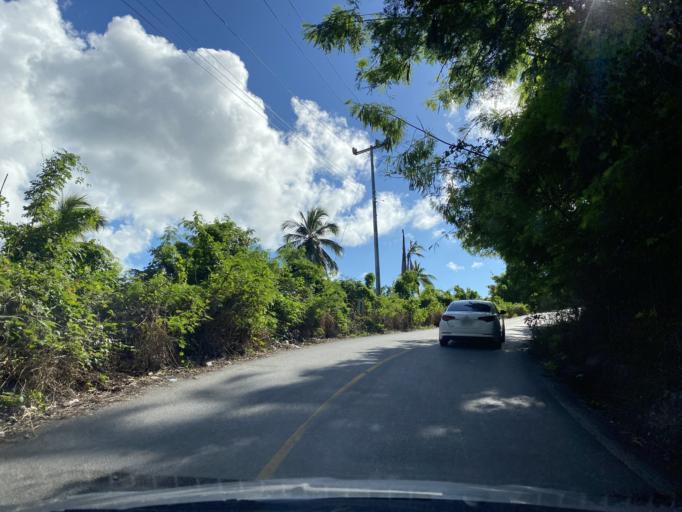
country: DO
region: Samana
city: Sanchez
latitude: 19.2376
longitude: -69.5966
